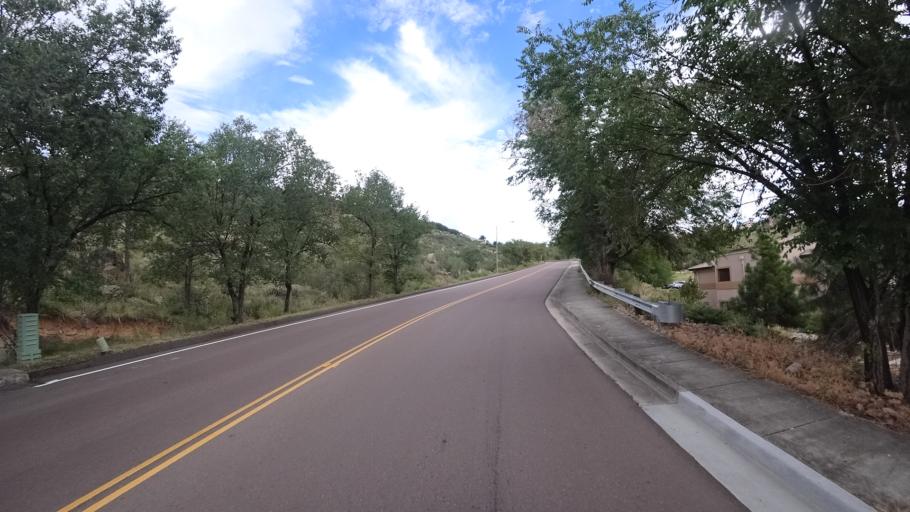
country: US
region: Colorado
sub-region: El Paso County
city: Colorado Springs
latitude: 38.9019
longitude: -104.8301
